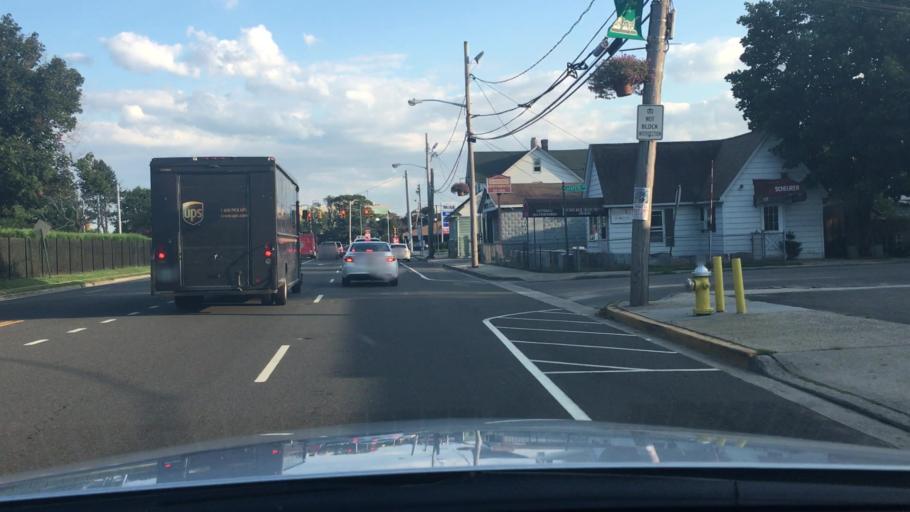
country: US
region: New York
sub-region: Nassau County
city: Westbury
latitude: 40.7487
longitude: -73.5878
